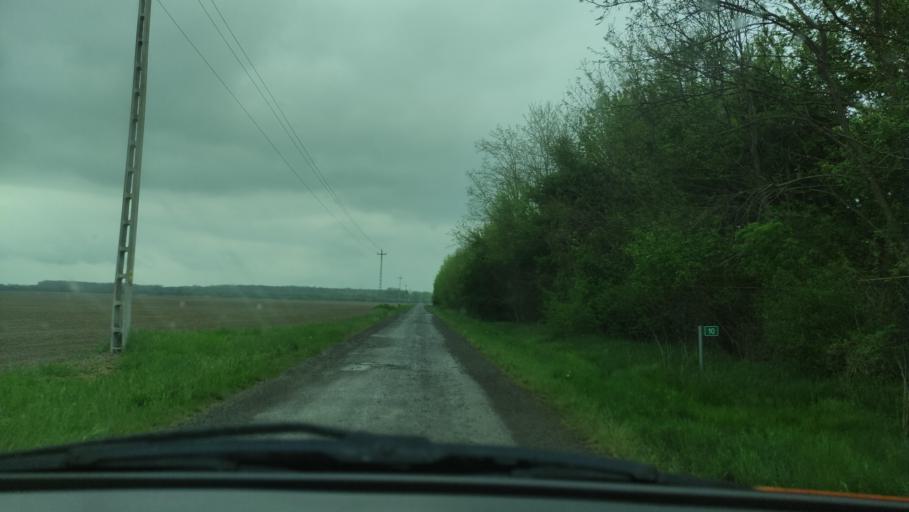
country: HR
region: Osjecko-Baranjska
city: Batina
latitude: 45.9006
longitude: 18.7772
